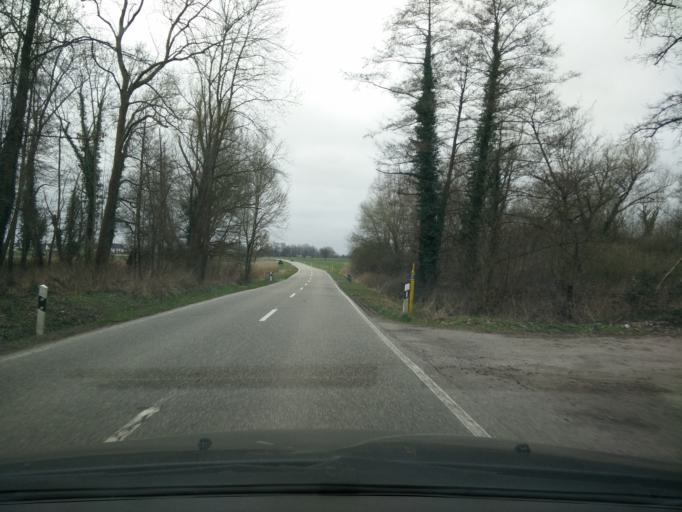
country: DE
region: Rheinland-Pfalz
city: Barbelroth
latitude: 49.1089
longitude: 8.0781
